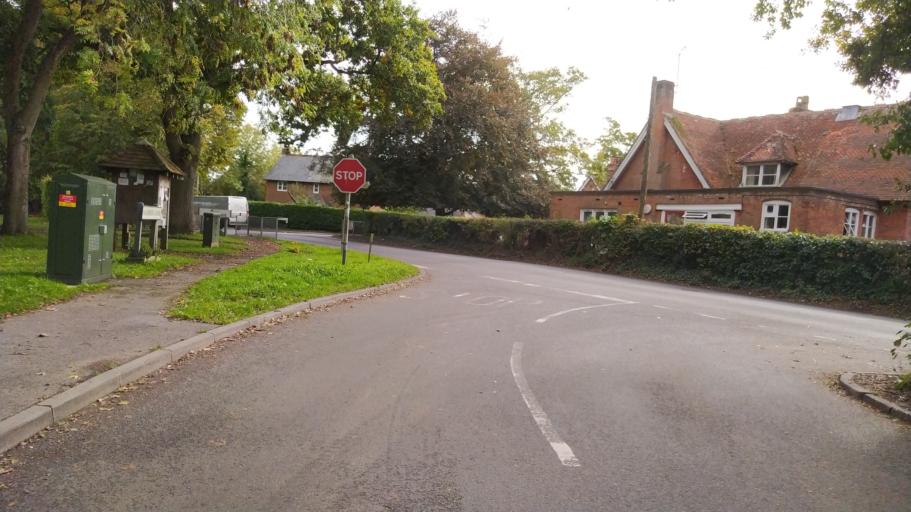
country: GB
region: England
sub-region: Hampshire
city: Romsey
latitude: 51.0163
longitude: -1.5451
